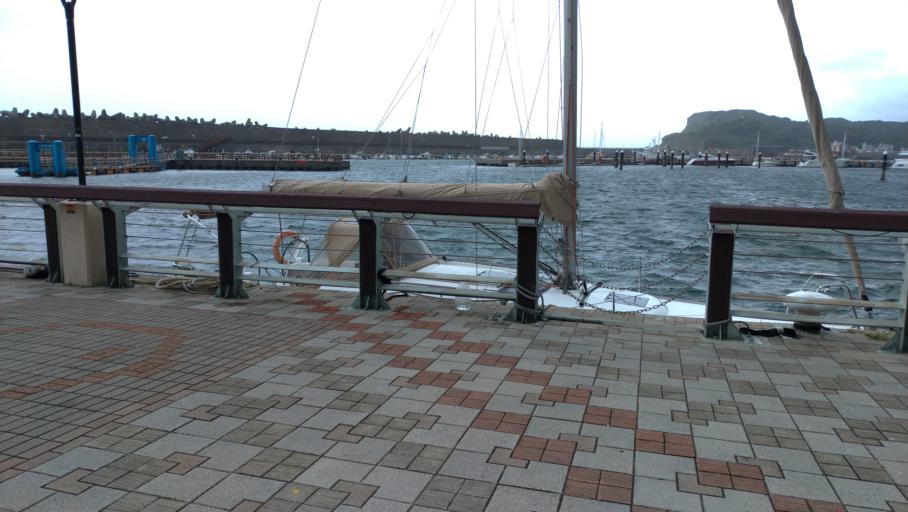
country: TW
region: Taiwan
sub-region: Keelung
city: Keelung
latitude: 25.1477
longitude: 121.7842
